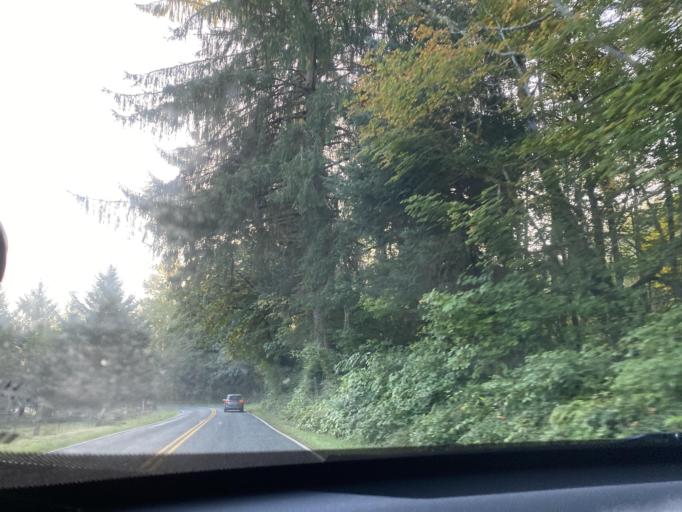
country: US
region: Washington
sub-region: Clallam County
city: Forks
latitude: 47.8162
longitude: -124.1659
